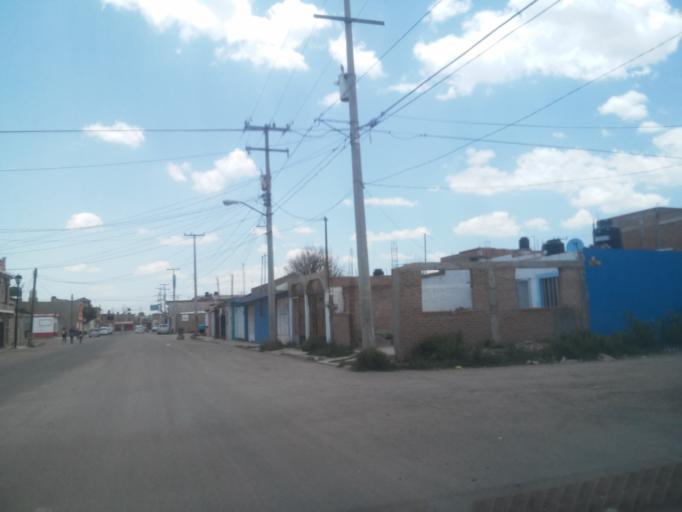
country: MX
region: Durango
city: Victoria de Durango
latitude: 24.0603
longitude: -104.6291
